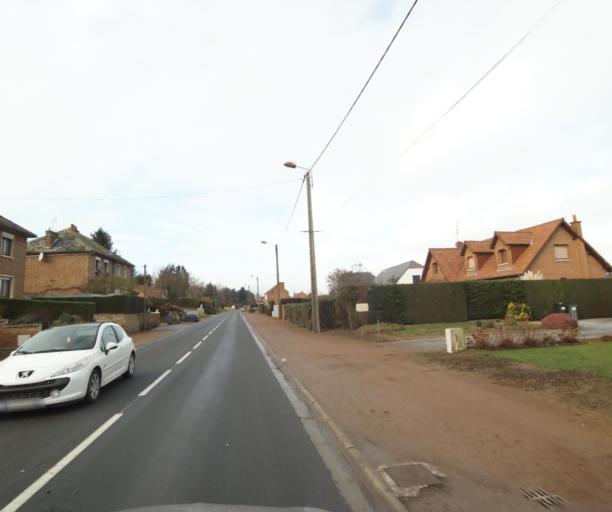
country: FR
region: Nord-Pas-de-Calais
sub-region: Departement du Nord
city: Saulzoir
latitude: 50.2677
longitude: 3.4676
